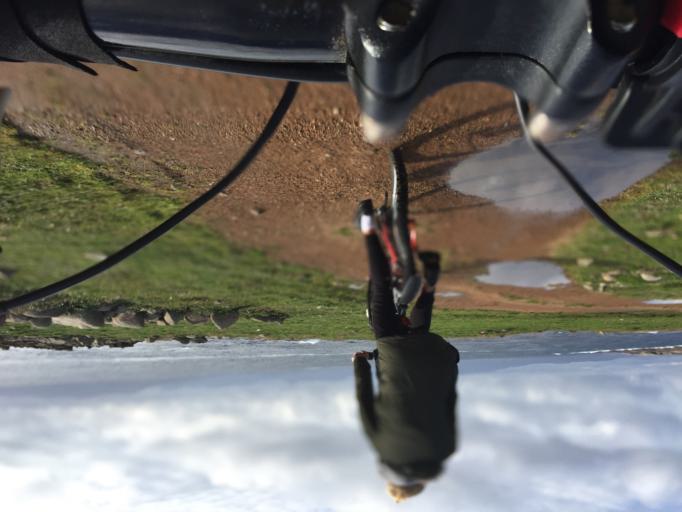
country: IE
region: Ulster
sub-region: County Donegal
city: Derrybeg
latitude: 55.2620
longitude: -8.2323
